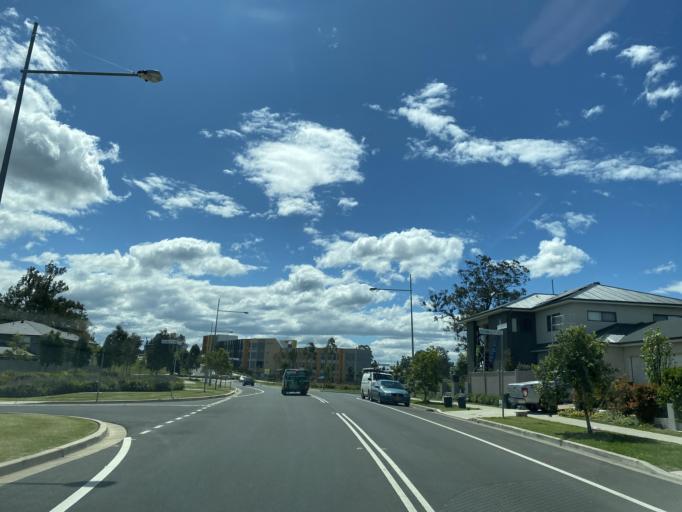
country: AU
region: New South Wales
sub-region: Camden
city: Narellan
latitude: -34.0144
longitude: 150.7771
